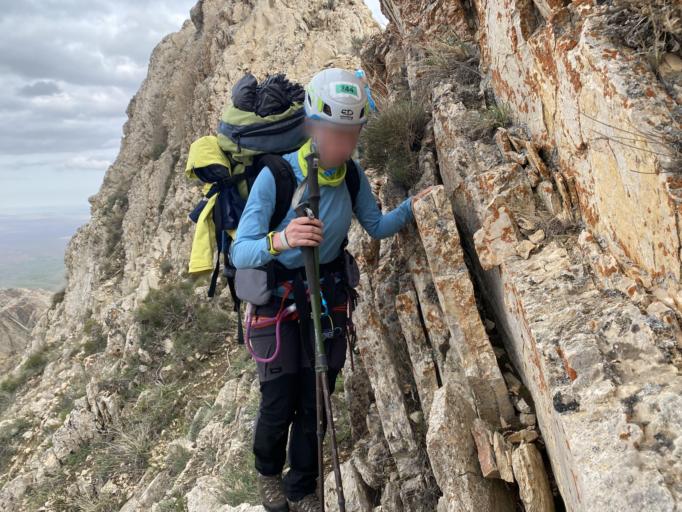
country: KZ
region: Ongtustik Qazaqstan
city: Ashchysay
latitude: 43.7569
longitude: 68.8154
